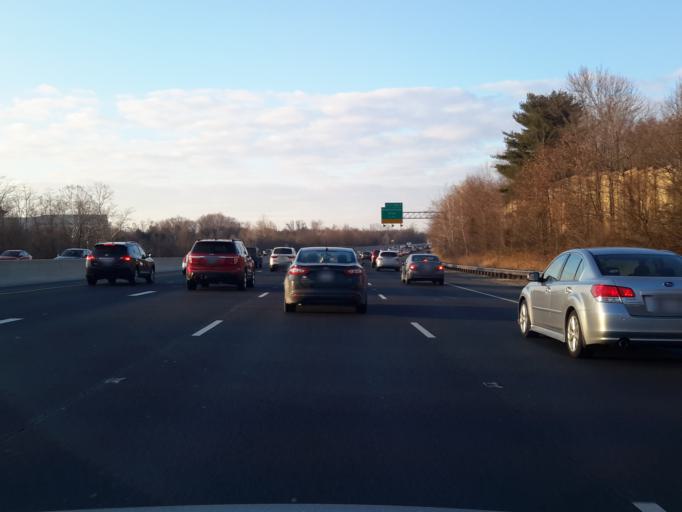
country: US
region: Maryland
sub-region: Montgomery County
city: Germantown
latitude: 39.1654
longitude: -77.2398
